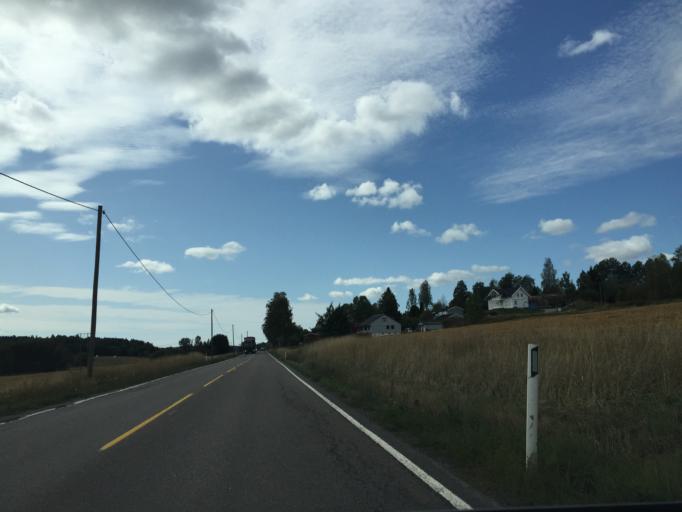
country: NO
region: Ostfold
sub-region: Hobol
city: Elvestad
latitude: 59.6129
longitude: 10.9310
